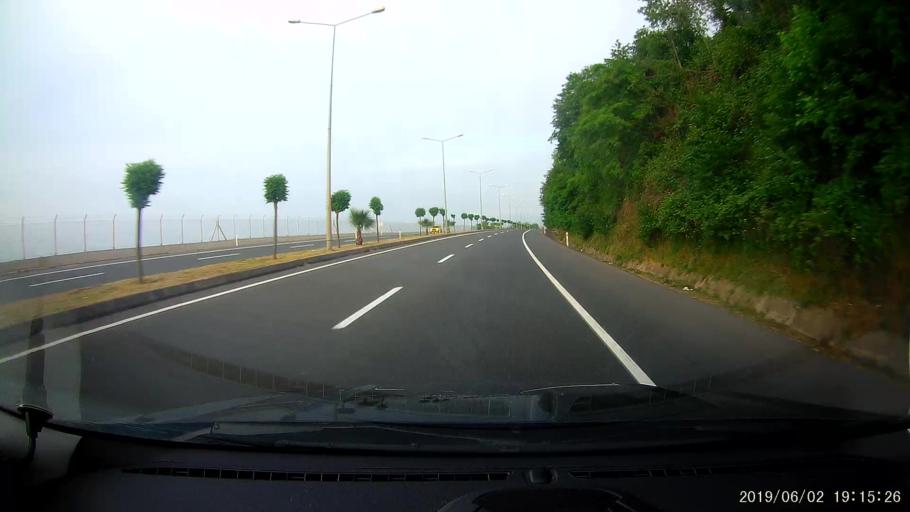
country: TR
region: Giresun
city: Piraziz
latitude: 40.9626
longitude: 38.0954
